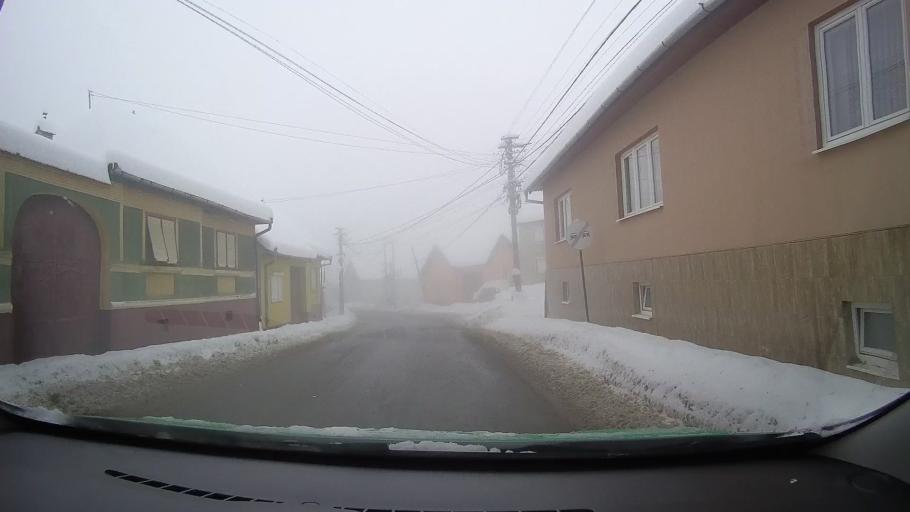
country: RO
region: Sibiu
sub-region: Comuna Jina
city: Jina
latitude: 45.7811
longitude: 23.6743
